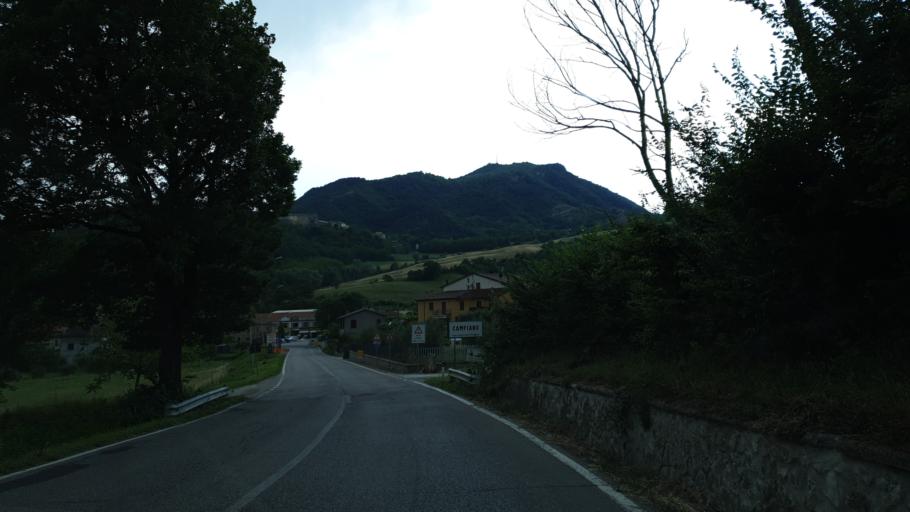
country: IT
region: Emilia-Romagna
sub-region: Provincia di Rimini
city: Talamello
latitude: 43.9091
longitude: 12.2966
